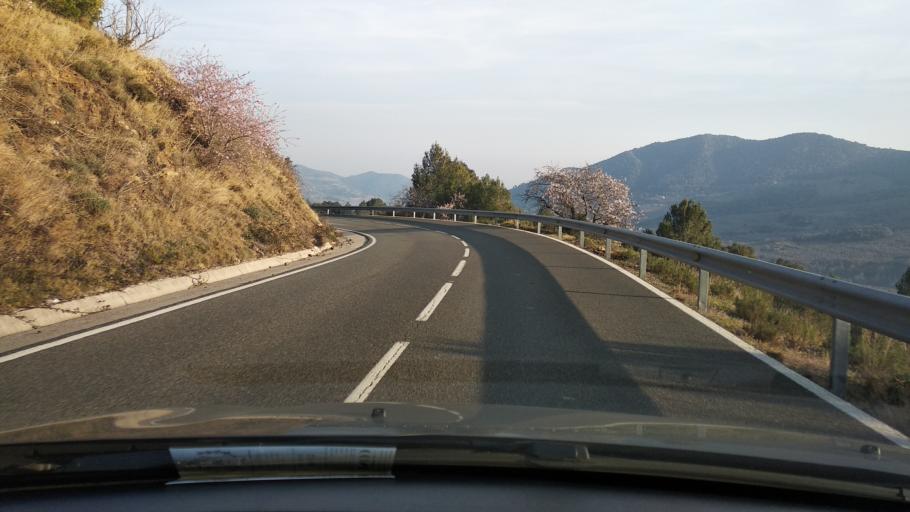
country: ES
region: Catalonia
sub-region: Provincia de Tarragona
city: Alforja
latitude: 41.2185
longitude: 0.9512
